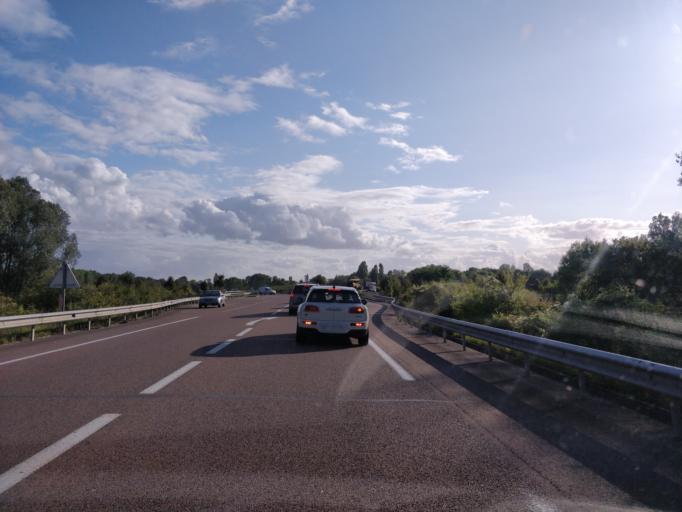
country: FR
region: Champagne-Ardenne
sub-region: Departement de l'Aube
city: Bucheres
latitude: 48.2518
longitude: 4.1132
